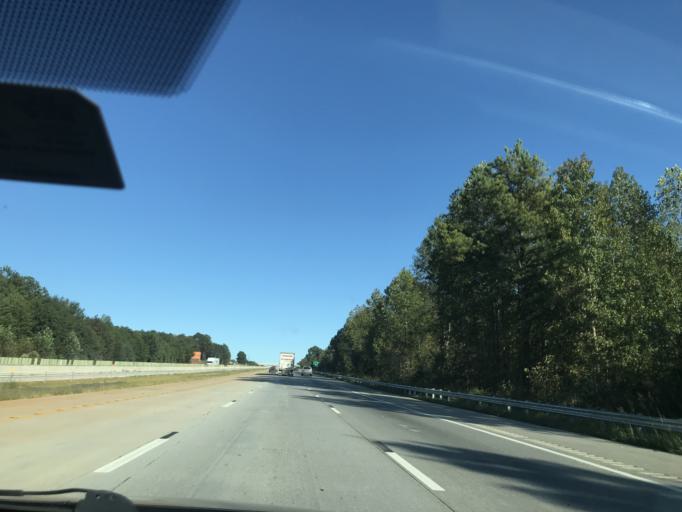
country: US
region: South Carolina
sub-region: Spartanburg County
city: Valley Falls
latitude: 35.0127
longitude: -81.9681
